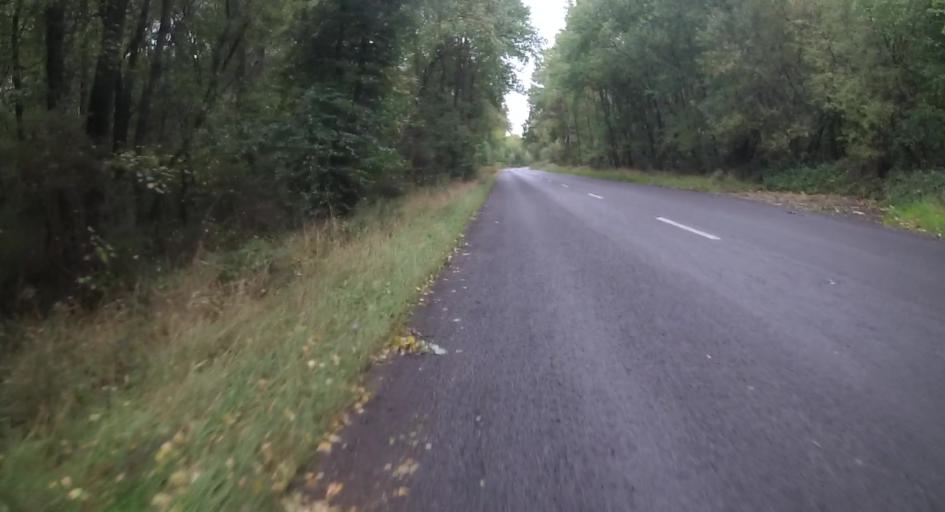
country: GB
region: England
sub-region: West Berkshire
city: Thatcham
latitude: 51.4207
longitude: -1.1930
